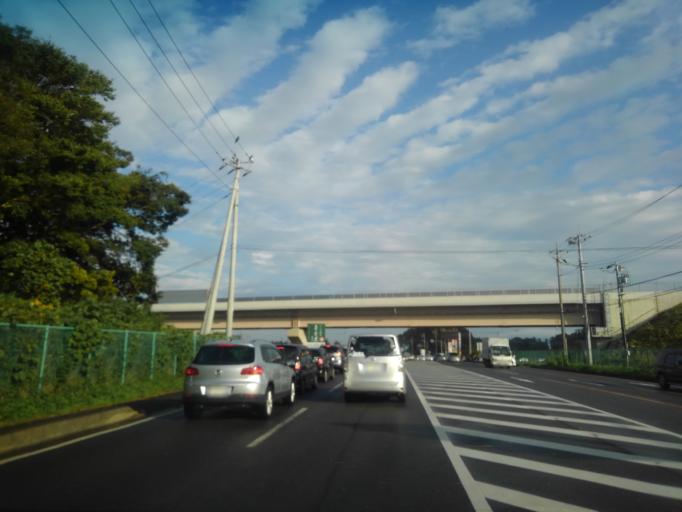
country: JP
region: Ibaraki
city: Naka
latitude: 36.0570
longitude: 140.0841
